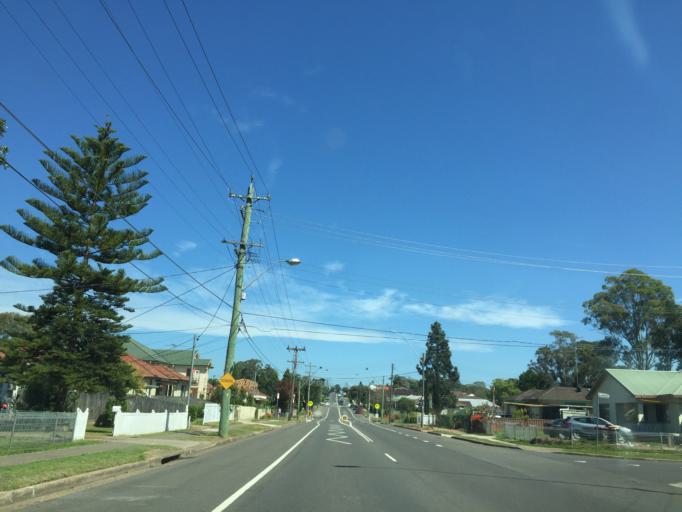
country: AU
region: New South Wales
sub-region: Blacktown
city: Blacktown
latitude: -33.7728
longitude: 150.8987
